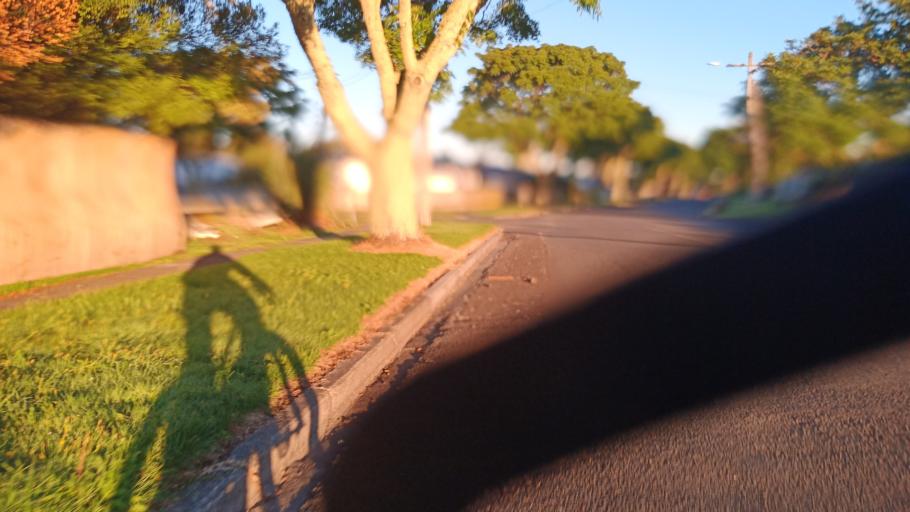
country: NZ
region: Gisborne
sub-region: Gisborne District
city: Gisborne
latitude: -38.6591
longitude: 177.9892
